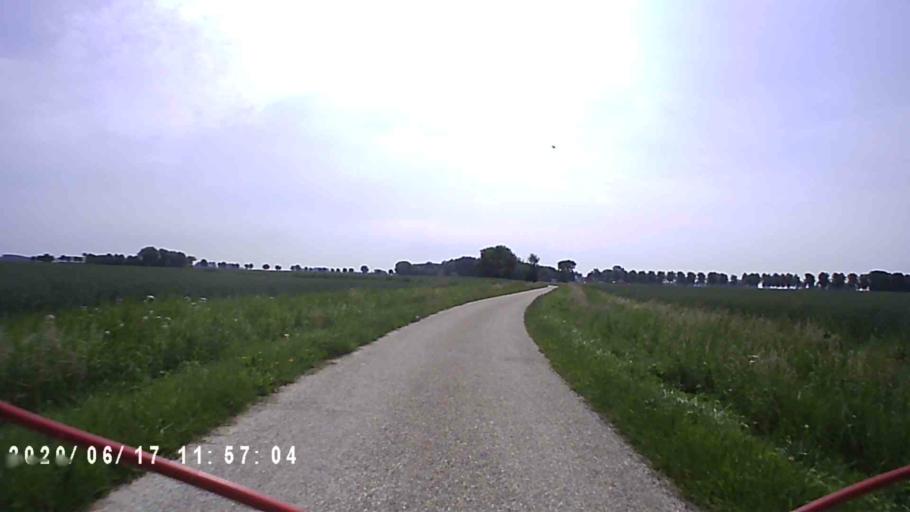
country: NL
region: Groningen
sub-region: Gemeente De Marne
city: Ulrum
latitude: 53.3475
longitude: 6.3224
